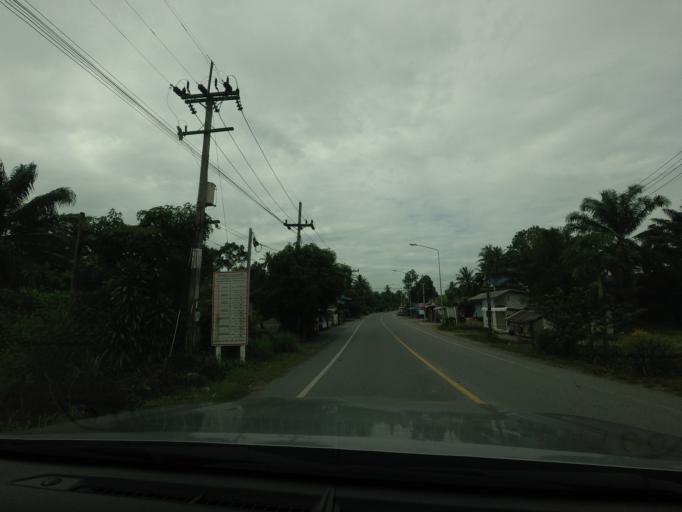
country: TH
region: Nakhon Si Thammarat
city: Phra Phrom
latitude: 8.3228
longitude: 99.9463
